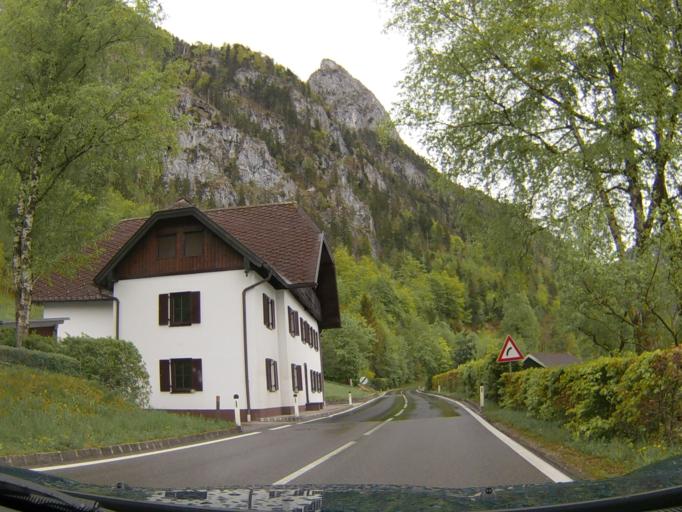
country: AT
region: Upper Austria
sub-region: Politischer Bezirk Vocklabruck
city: Steinbach am Attersee
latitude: 47.8066
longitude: 13.5480
